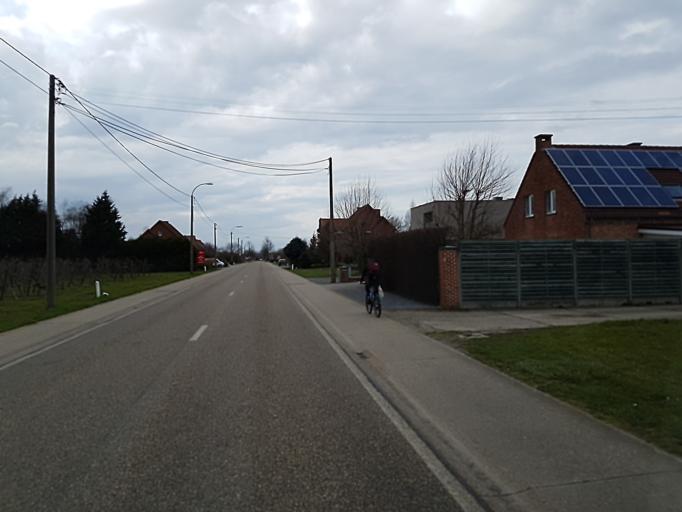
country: BE
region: Flanders
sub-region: Provincie Limburg
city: Nieuwerkerken
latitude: 50.9185
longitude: 5.2360
